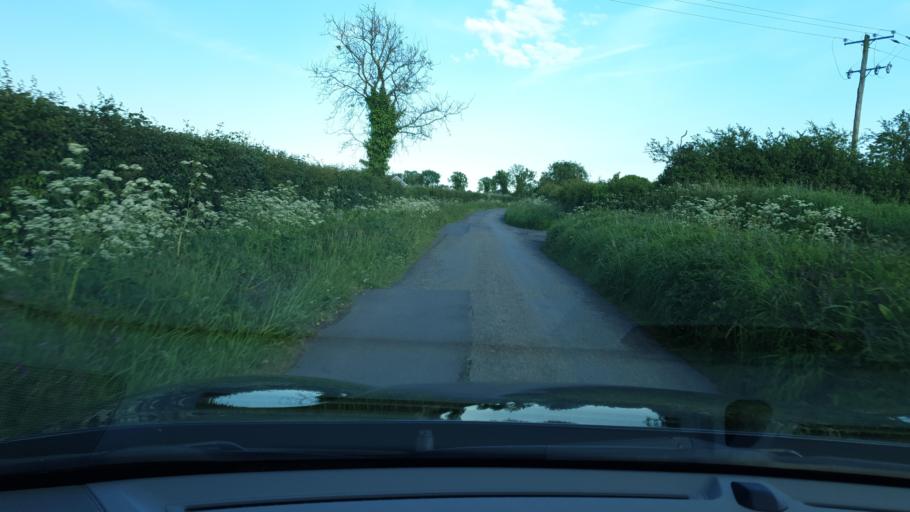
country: IE
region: Leinster
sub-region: An Mhi
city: Ashbourne
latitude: 53.5540
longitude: -6.3623
